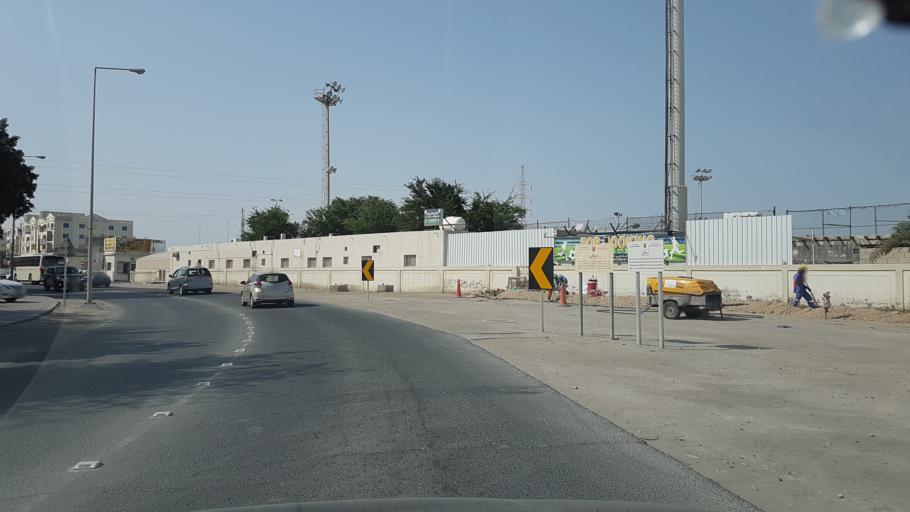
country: BH
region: Northern
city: Madinat `Isa
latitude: 26.1757
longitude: 50.5373
